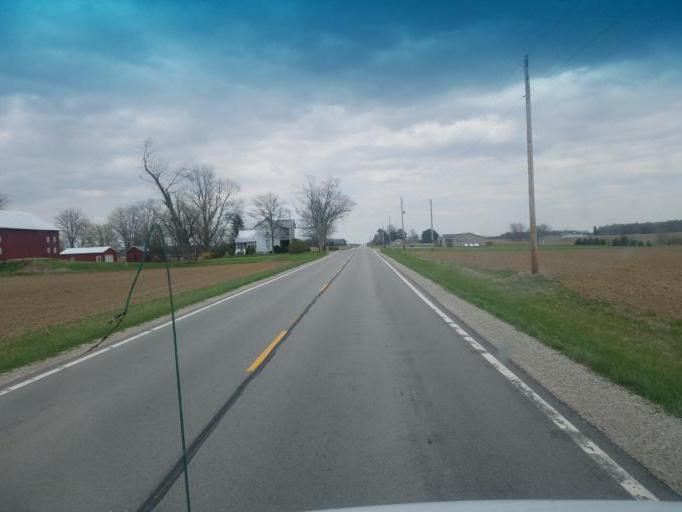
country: US
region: Ohio
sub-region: Seneca County
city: Tiffin
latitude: 40.9500
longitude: -83.1042
